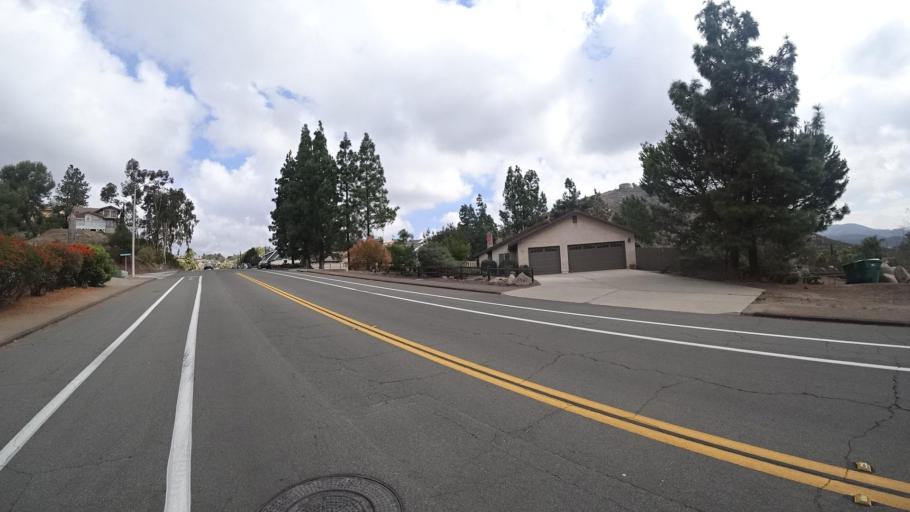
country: US
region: California
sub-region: San Diego County
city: Granite Hills
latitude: 32.7697
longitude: -116.9099
